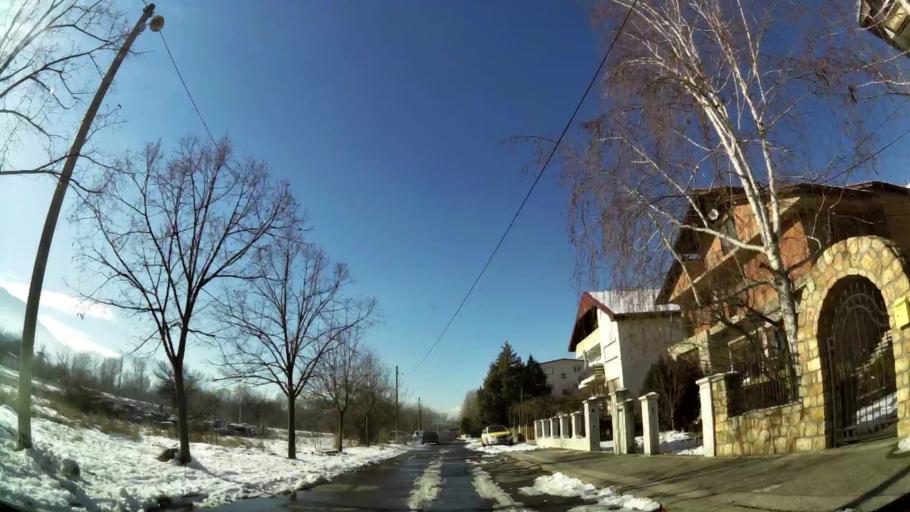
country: MK
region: Saraj
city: Saraj
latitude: 42.0040
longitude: 21.3497
